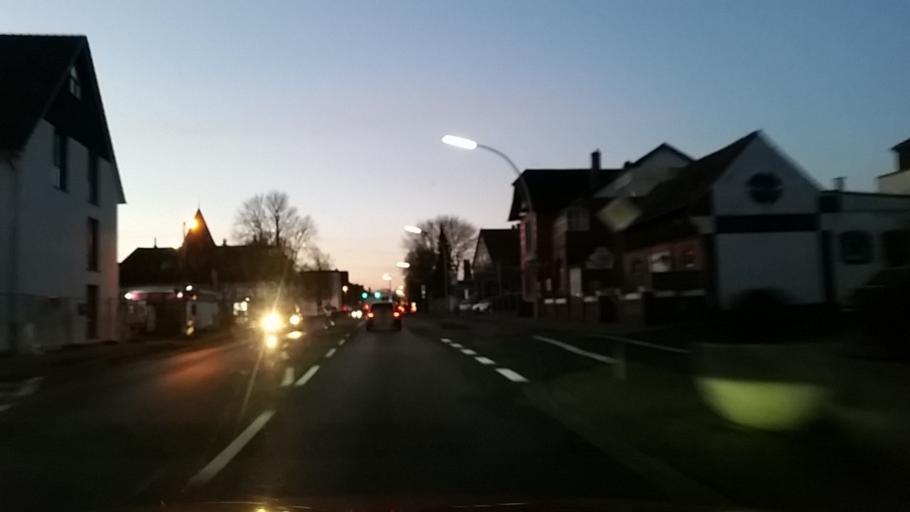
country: DE
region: Lower Saxony
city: Leiferde
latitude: 52.2252
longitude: 10.5039
